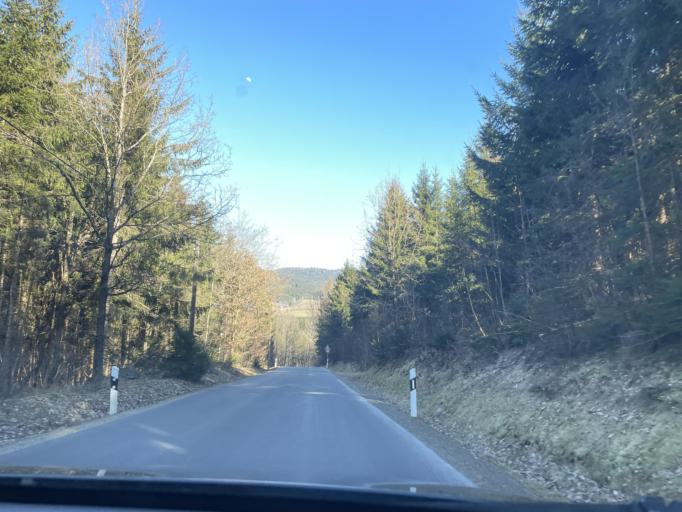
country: DE
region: Bavaria
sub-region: Lower Bavaria
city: Geiersthal
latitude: 49.0750
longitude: 12.9824
